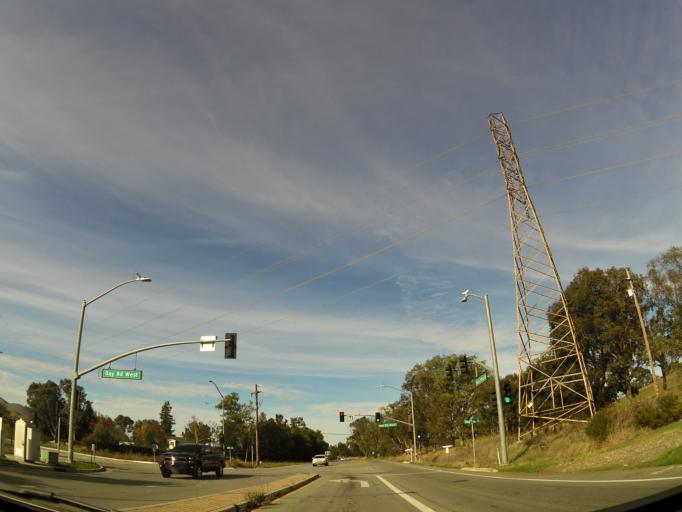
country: US
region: California
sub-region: Santa Clara County
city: Gilroy
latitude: 37.0375
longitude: -121.5976
